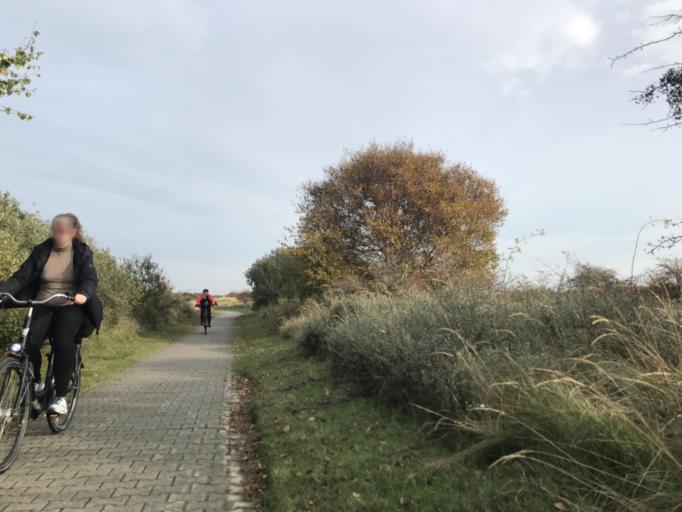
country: DE
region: Lower Saxony
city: Borkum
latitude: 53.6043
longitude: 6.7531
